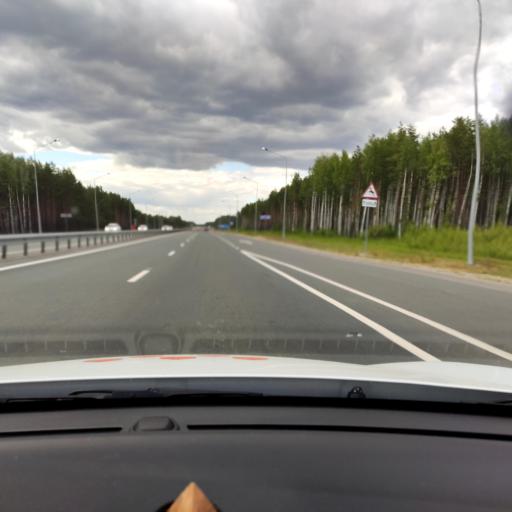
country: RU
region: Mariy-El
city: Surok
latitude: 56.4469
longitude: 48.1056
